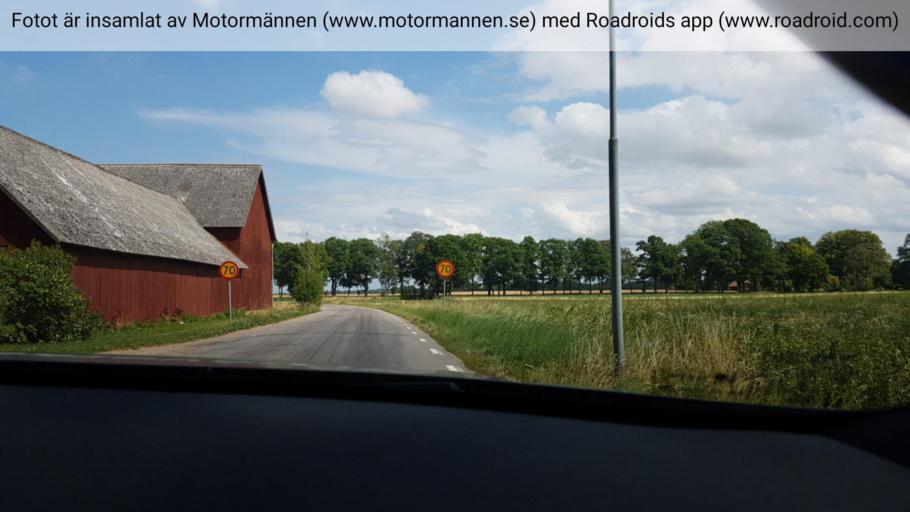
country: SE
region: Vaestra Goetaland
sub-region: Gotene Kommun
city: Kallby
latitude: 58.4729
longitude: 13.3331
